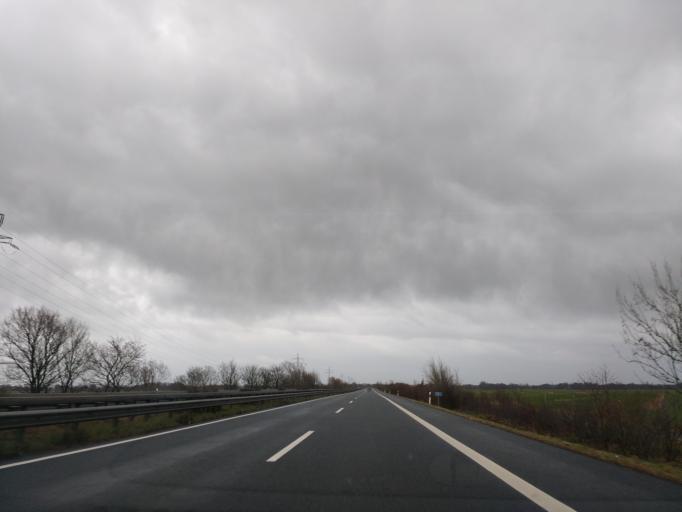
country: DE
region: Lower Saxony
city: Cuxhaven
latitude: 53.8010
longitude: 8.7072
